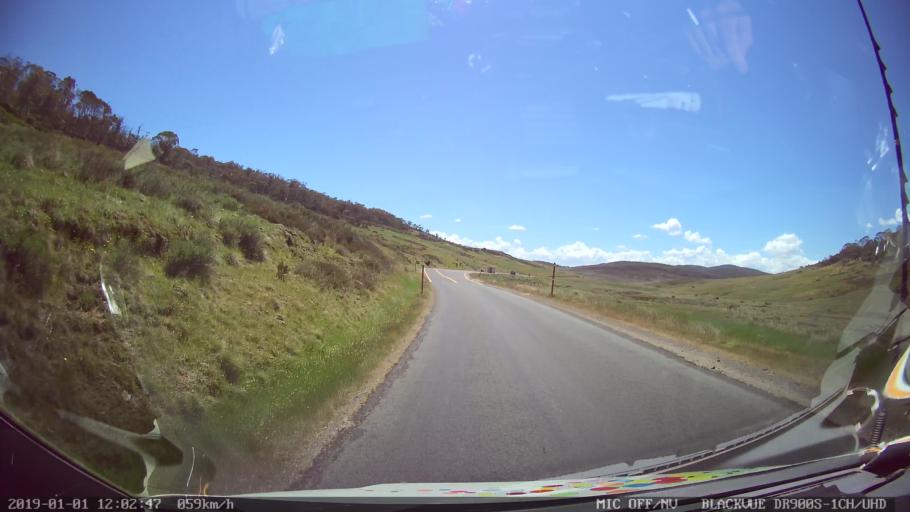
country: AU
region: New South Wales
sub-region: Snowy River
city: Jindabyne
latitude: -35.8710
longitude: 148.4804
